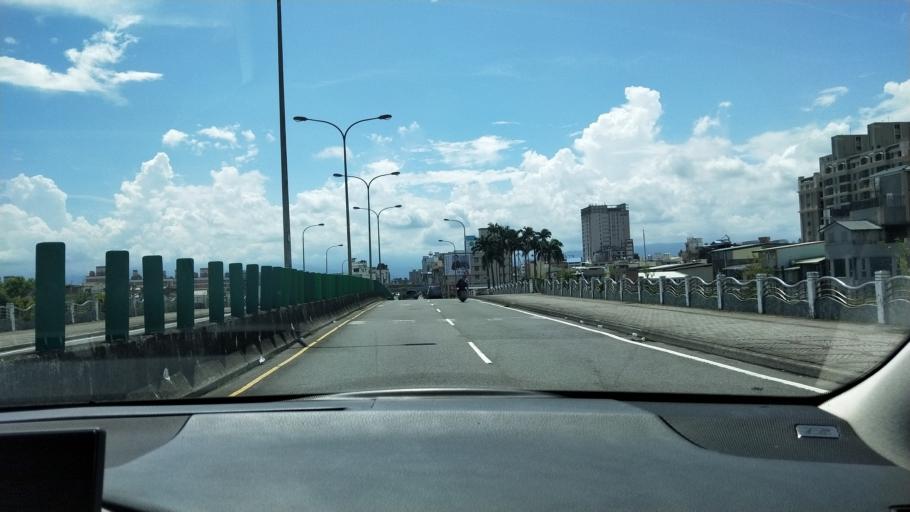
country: TW
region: Taiwan
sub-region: Yilan
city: Yilan
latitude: 24.7633
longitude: 121.7609
